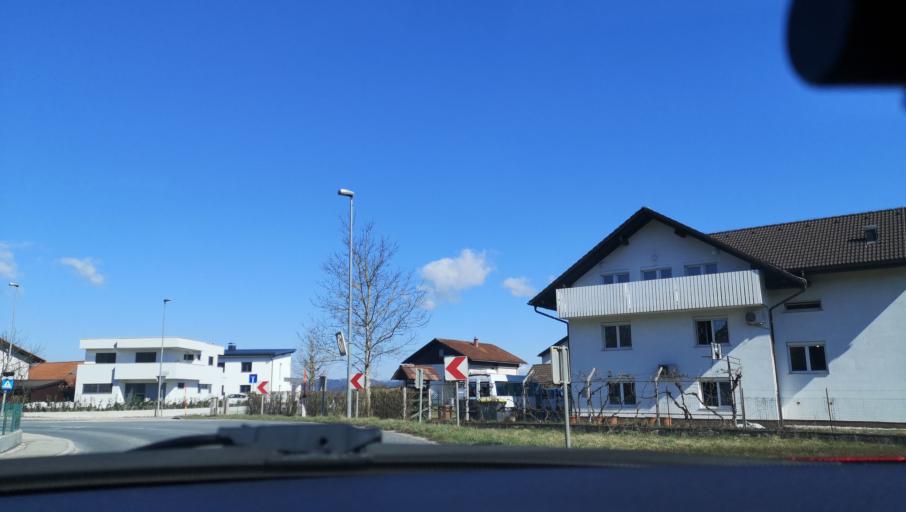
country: SI
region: Ig
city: Ig
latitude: 45.9605
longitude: 14.5313
